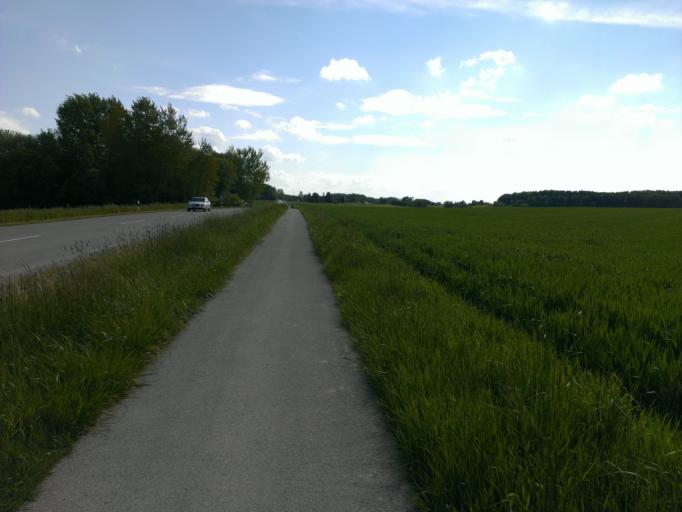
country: DE
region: Bavaria
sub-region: Upper Bavaria
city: Schaftlarn
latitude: 48.0206
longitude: 11.4163
